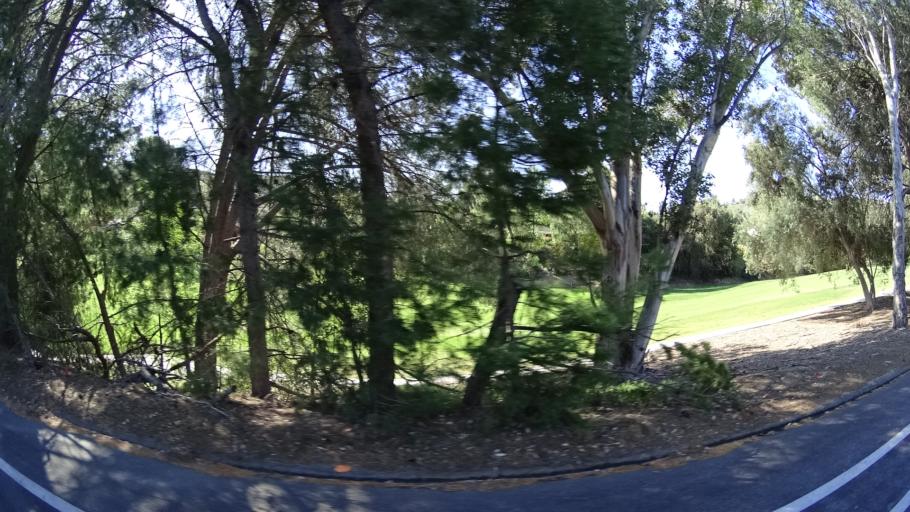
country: US
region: California
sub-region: Ventura County
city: Moorpark
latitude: 34.2396
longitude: -118.8446
